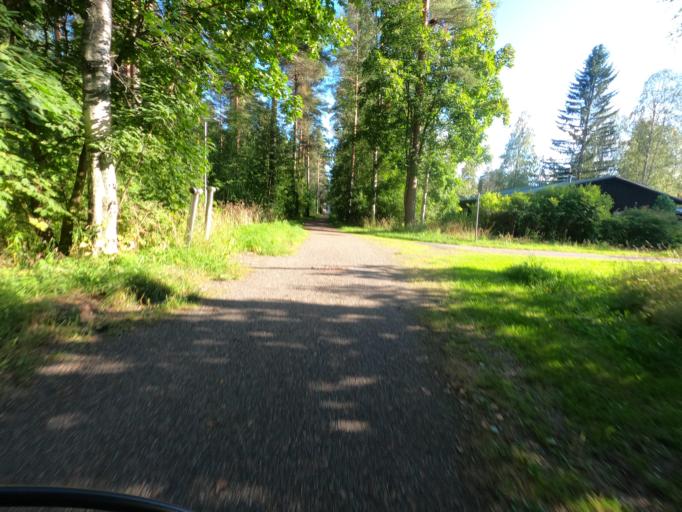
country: FI
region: North Karelia
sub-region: Joensuu
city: Joensuu
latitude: 62.6139
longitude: 29.7581
